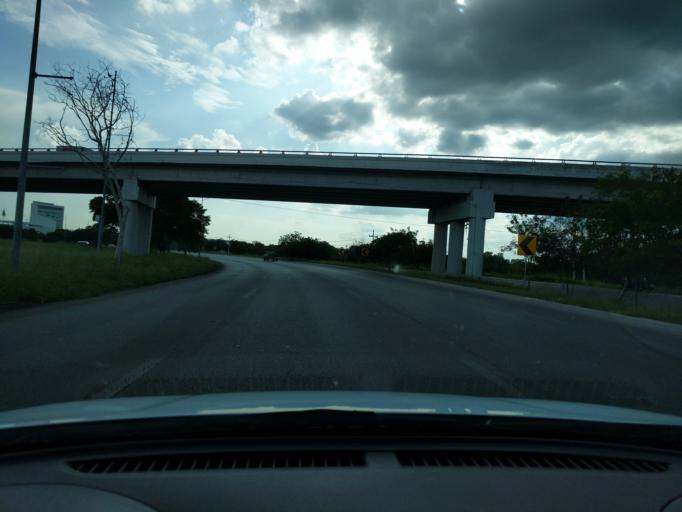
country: MX
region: Yucatan
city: Caucel
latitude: 20.9774
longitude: -89.6881
